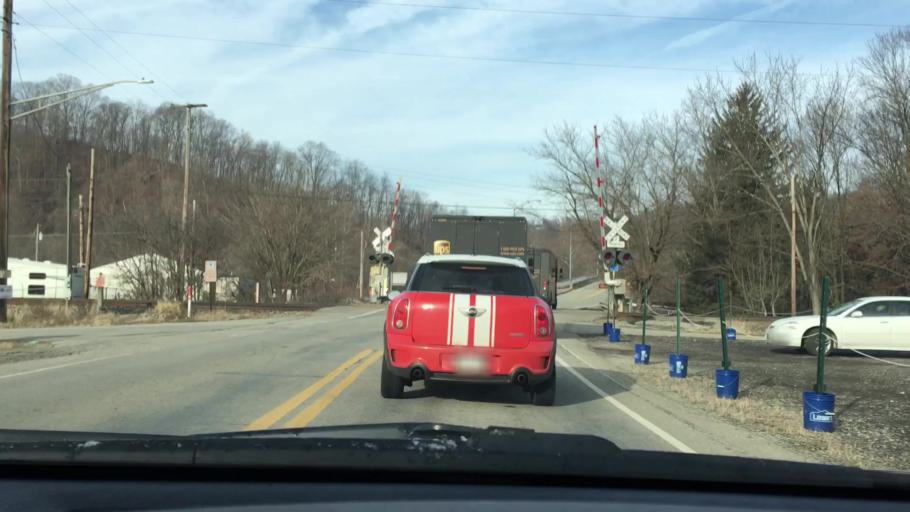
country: US
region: Pennsylvania
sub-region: Allegheny County
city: Industry
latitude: 40.2398
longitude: -79.8031
